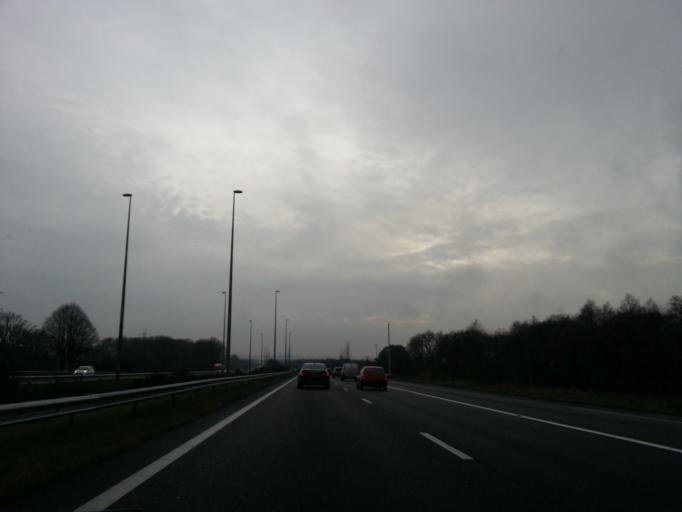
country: NL
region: Gelderland
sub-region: Gemeente Rozendaal
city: Rozendaal
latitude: 52.0616
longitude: 5.9416
